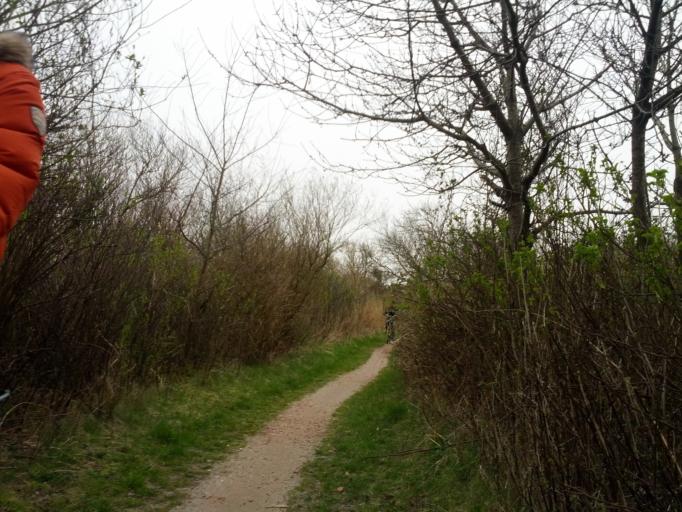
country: DE
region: Lower Saxony
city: Langeoog
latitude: 53.7383
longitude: 7.4709
